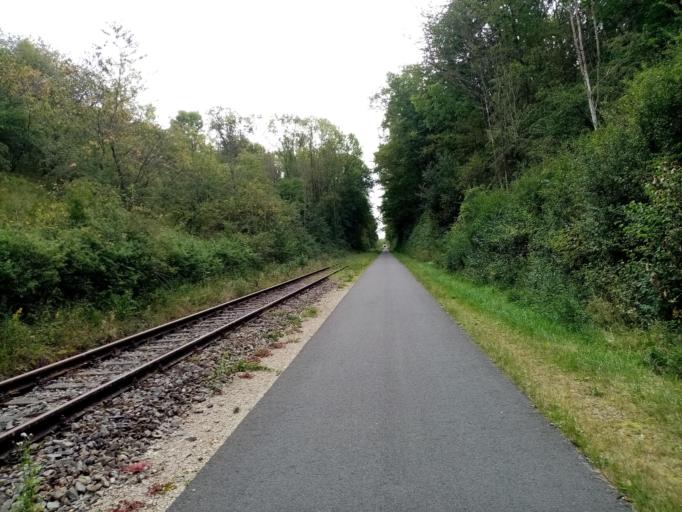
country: DE
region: Thuringia
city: Dingelstadt
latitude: 51.3080
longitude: 10.3012
